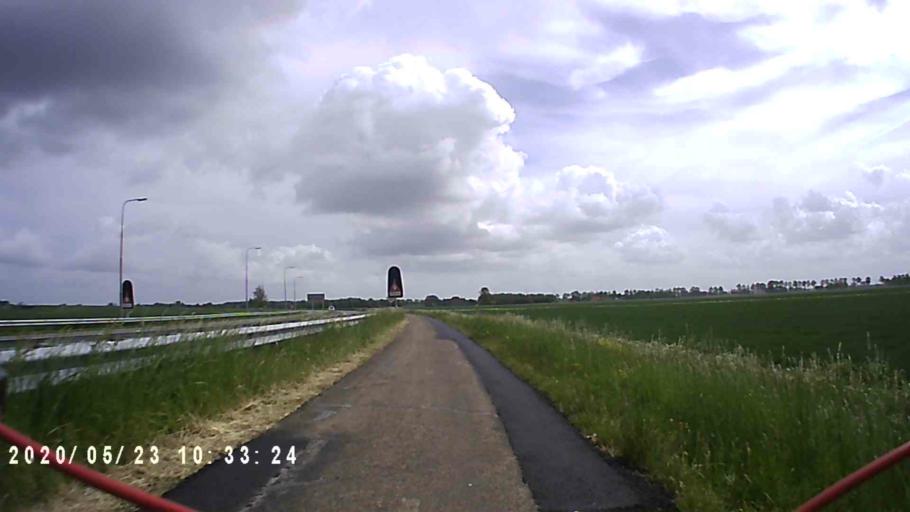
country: NL
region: Groningen
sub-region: Gemeente Appingedam
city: Appingedam
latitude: 53.3041
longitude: 6.8821
